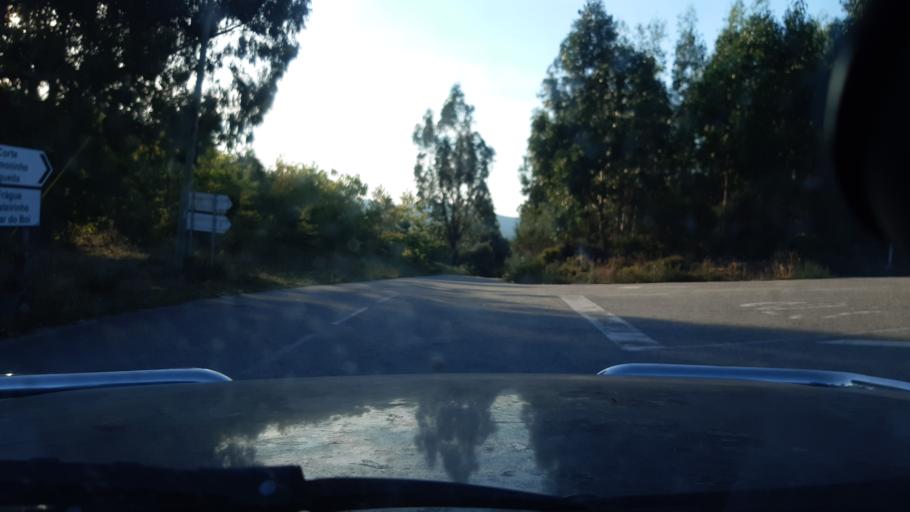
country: PT
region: Viseu
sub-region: Mortagua
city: Mortagua
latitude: 40.5409
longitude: -8.2506
